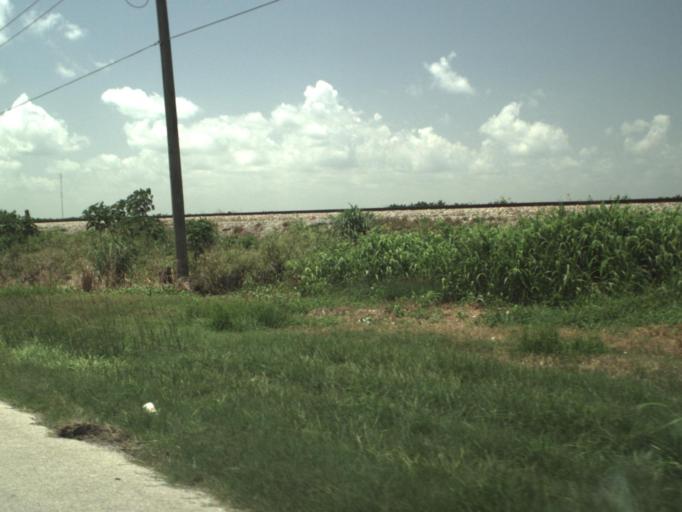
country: US
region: Florida
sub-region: Palm Beach County
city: Pahokee
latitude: 26.8240
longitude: -80.6472
